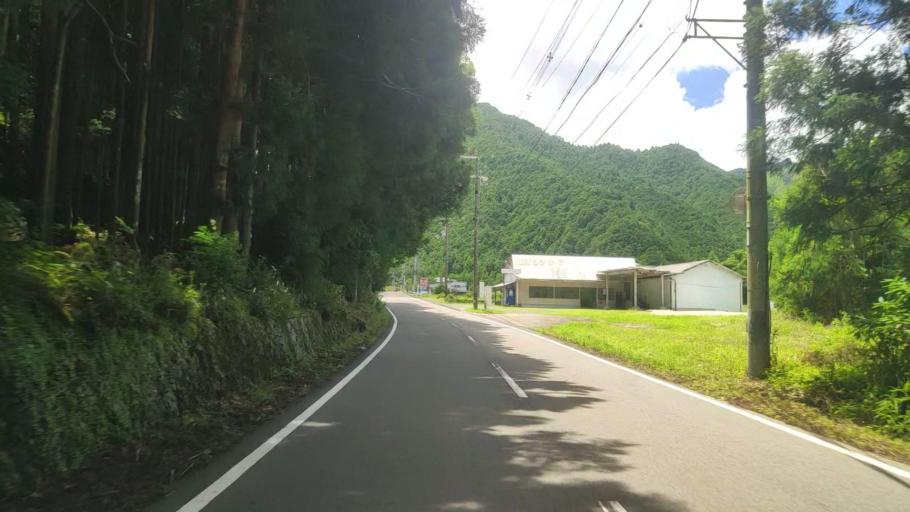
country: JP
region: Mie
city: Owase
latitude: 33.9665
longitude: 136.0611
